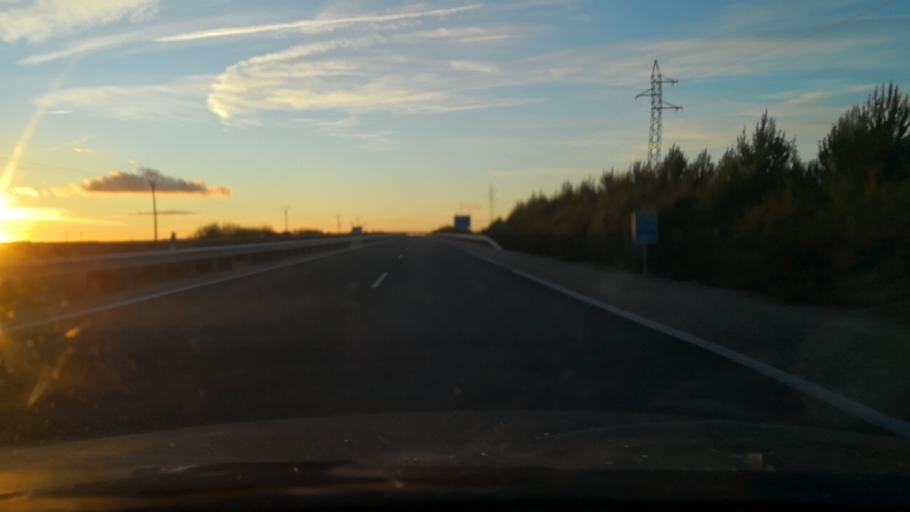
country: ES
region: Castille and Leon
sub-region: Provincia de Valladolid
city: Torrecilla de la Abadesa
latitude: 41.5055
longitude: -5.0554
